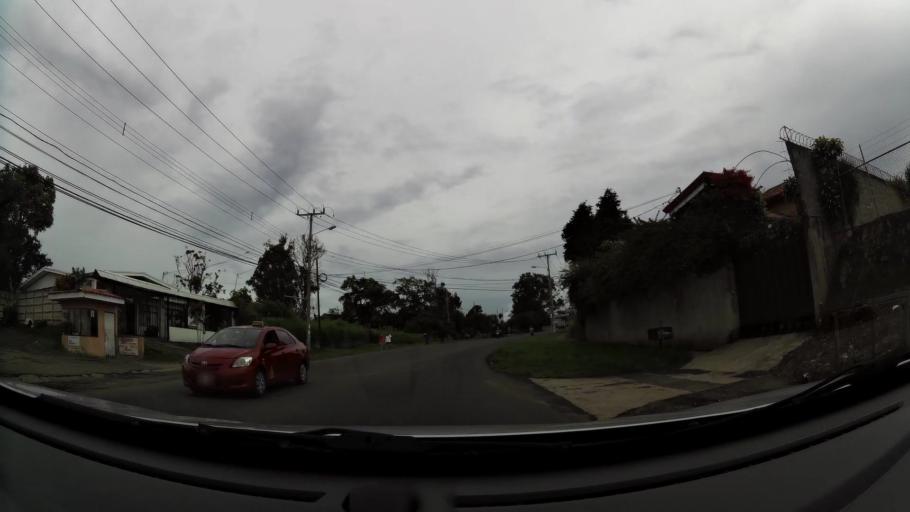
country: CR
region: San Jose
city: Ipis
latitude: 9.9730
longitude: -84.0118
